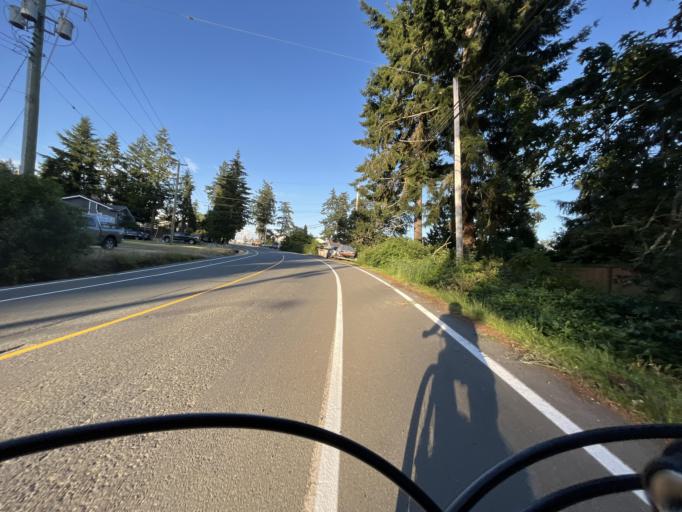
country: CA
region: British Columbia
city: Langford
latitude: 48.4491
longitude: -123.5220
